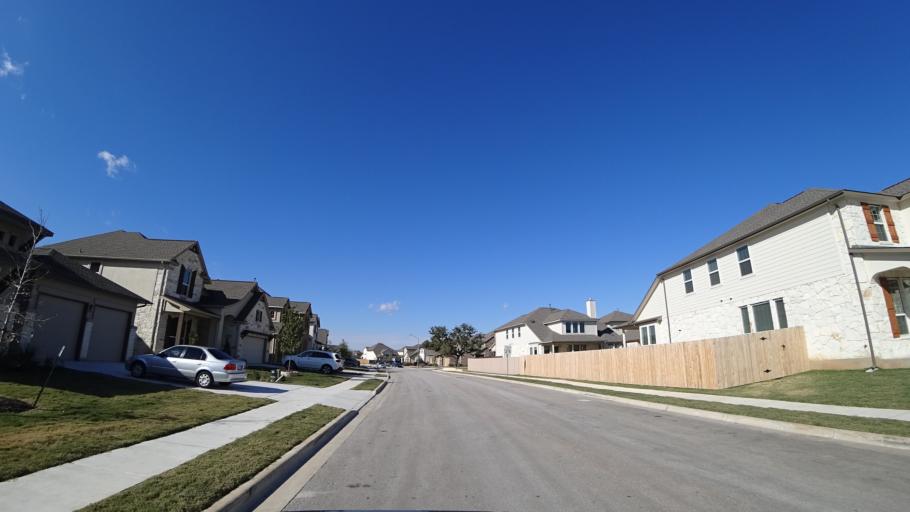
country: US
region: Texas
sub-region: Williamson County
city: Brushy Creek
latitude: 30.4914
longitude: -97.7220
